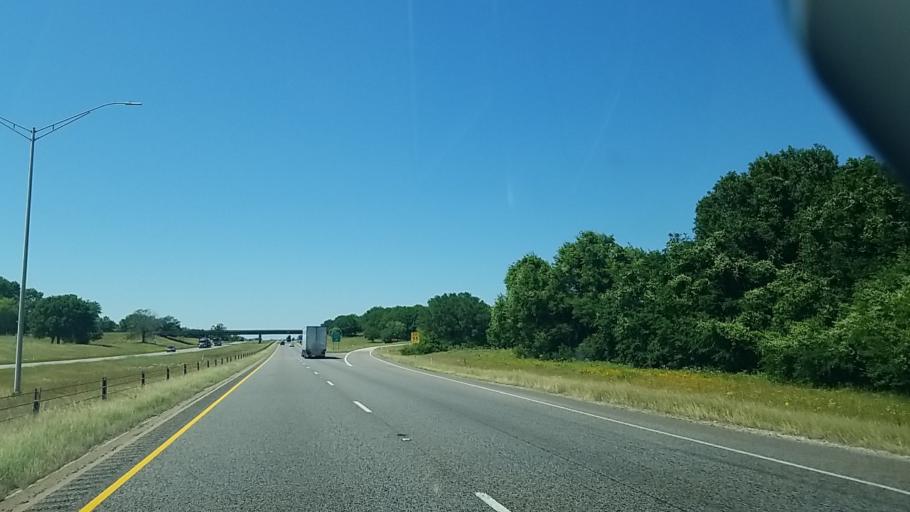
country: US
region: Texas
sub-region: Freestone County
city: Fairfield
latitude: 31.7111
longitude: -96.1753
